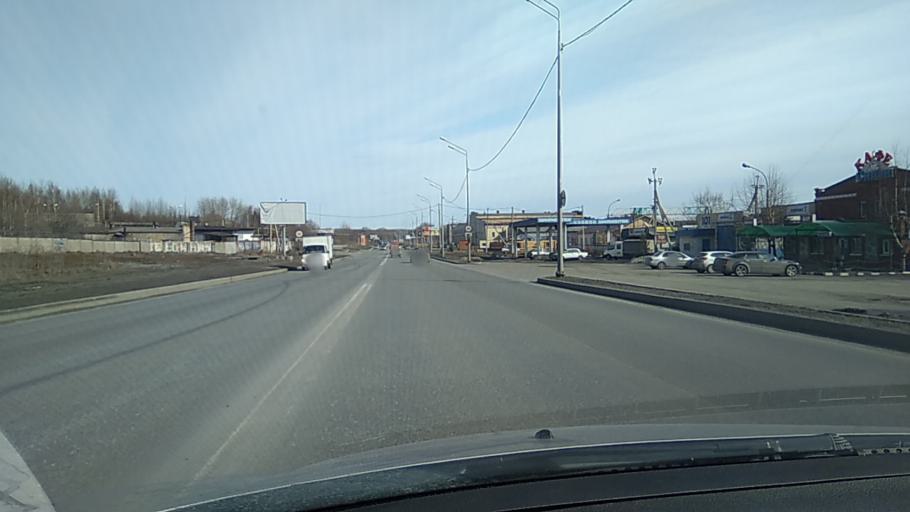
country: RU
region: Sverdlovsk
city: Nizhniy Tagil
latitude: 57.9090
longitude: 60.0261
